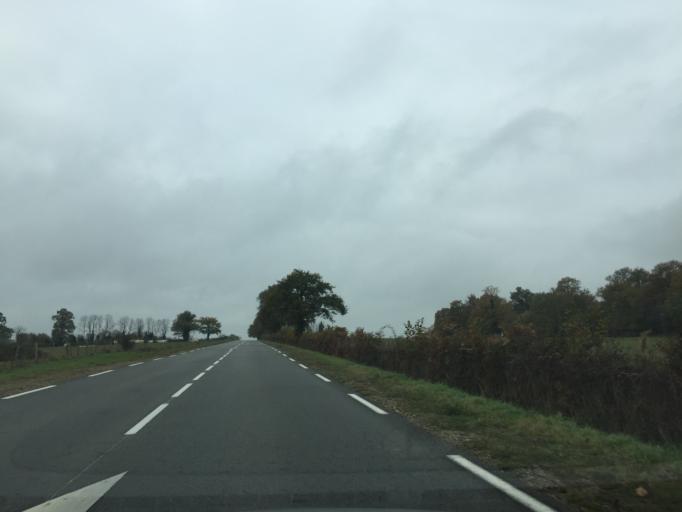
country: FR
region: Limousin
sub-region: Departement de la Creuse
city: Gouzon
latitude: 46.1327
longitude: 2.1927
